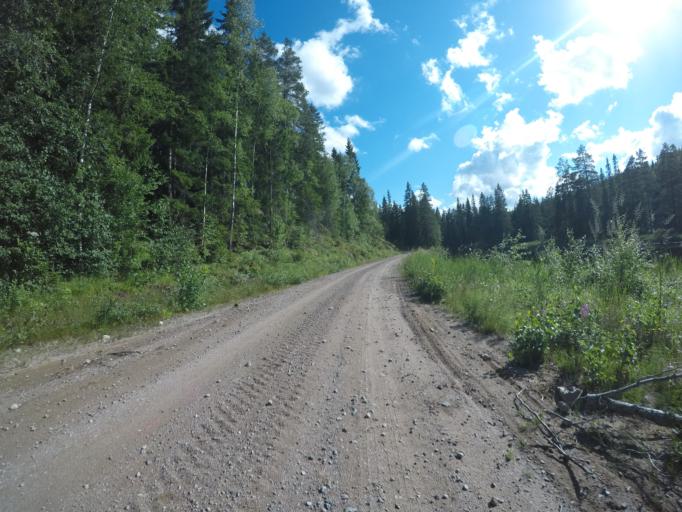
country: SE
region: Dalarna
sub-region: Ludvika Kommun
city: Abborrberget
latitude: 60.0103
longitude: 14.6100
